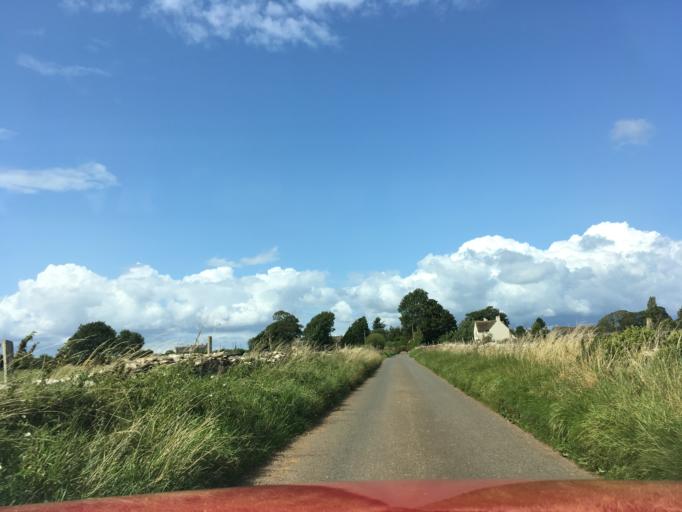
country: GB
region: England
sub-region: Wiltshire
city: Luckington
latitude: 51.6144
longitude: -2.2552
